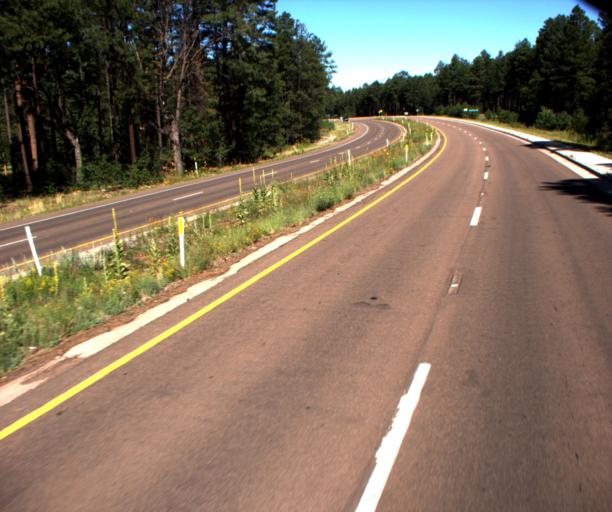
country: US
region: Arizona
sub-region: Navajo County
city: Pinetop-Lakeside
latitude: 34.1202
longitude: -109.9175
